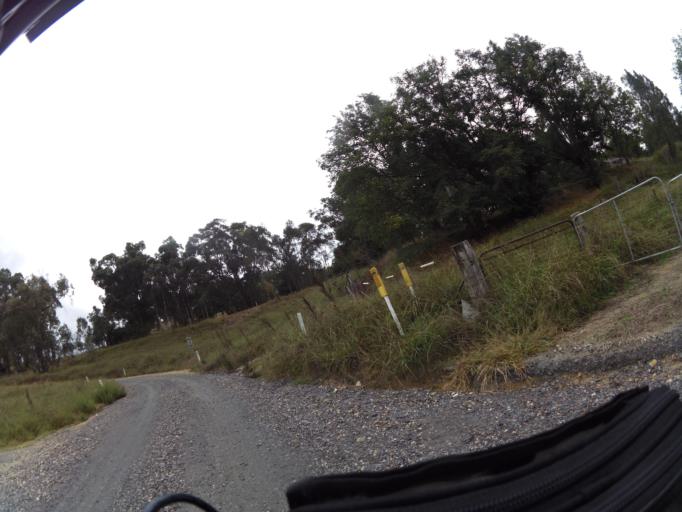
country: AU
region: New South Wales
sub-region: Albury Municipality
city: East Albury
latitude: -36.1943
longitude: 147.3106
